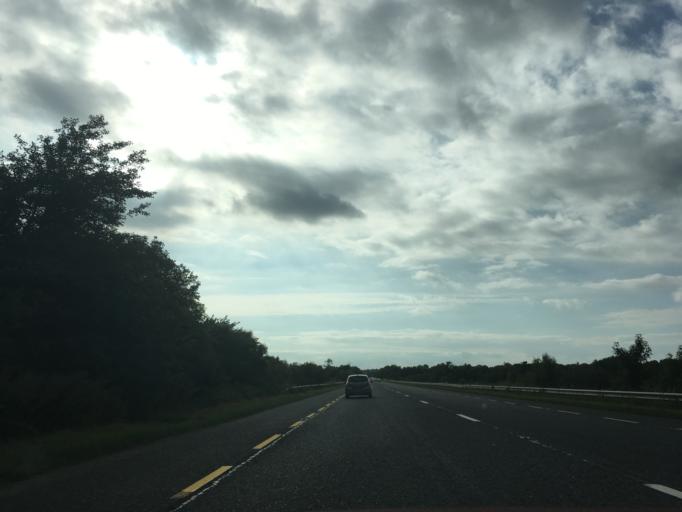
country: IE
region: Leinster
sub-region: Loch Garman
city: Loch Garman
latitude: 52.3467
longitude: -6.6066
